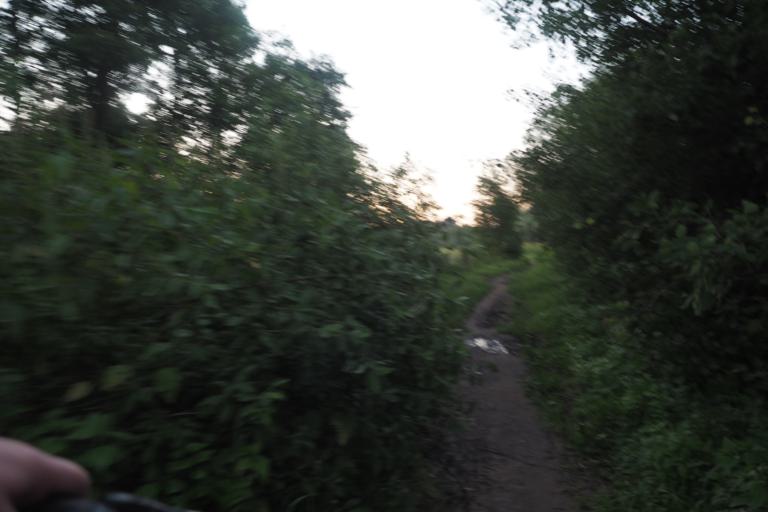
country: RU
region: Moskovskaya
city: Ramenskoye
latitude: 55.5496
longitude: 38.3014
